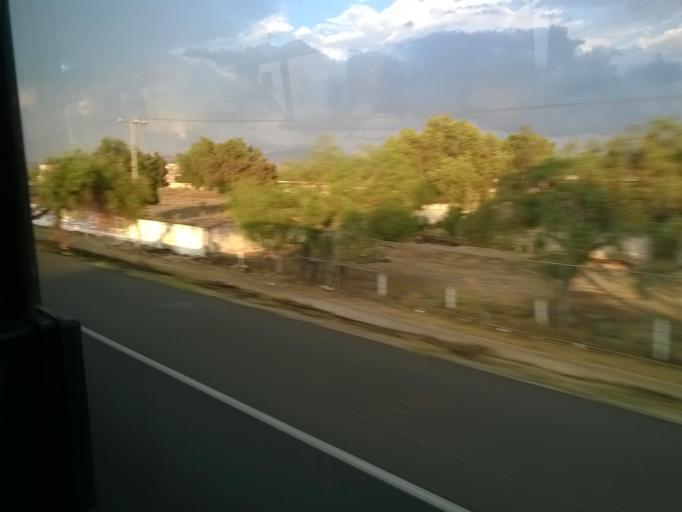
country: MX
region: Mexico
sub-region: Tecamac
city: Tecamac de Felipe Villanueva
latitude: 19.7134
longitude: -98.9631
